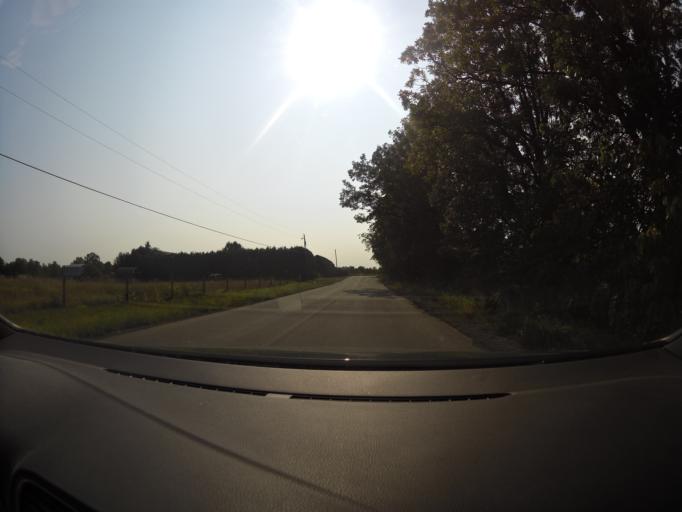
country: CA
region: Ontario
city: Carleton Place
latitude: 45.2855
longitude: -76.1576
